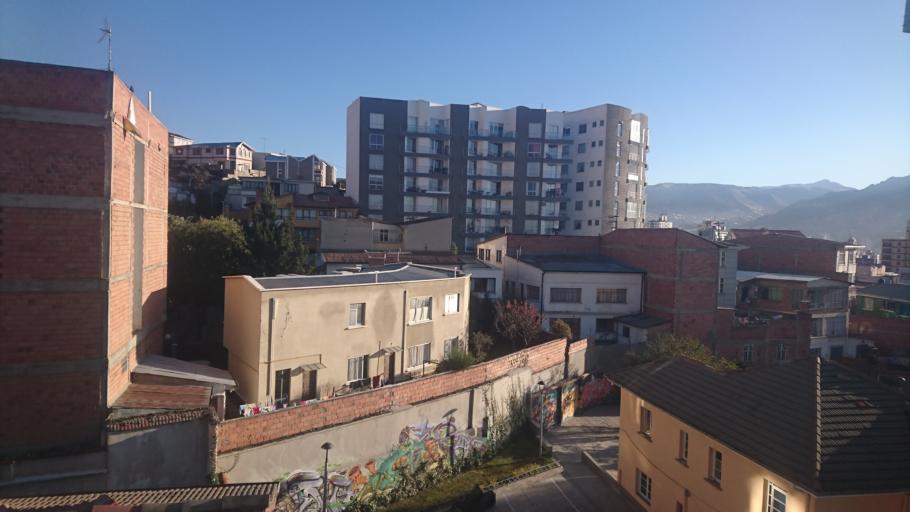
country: BO
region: La Paz
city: La Paz
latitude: -16.5147
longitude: -68.1308
